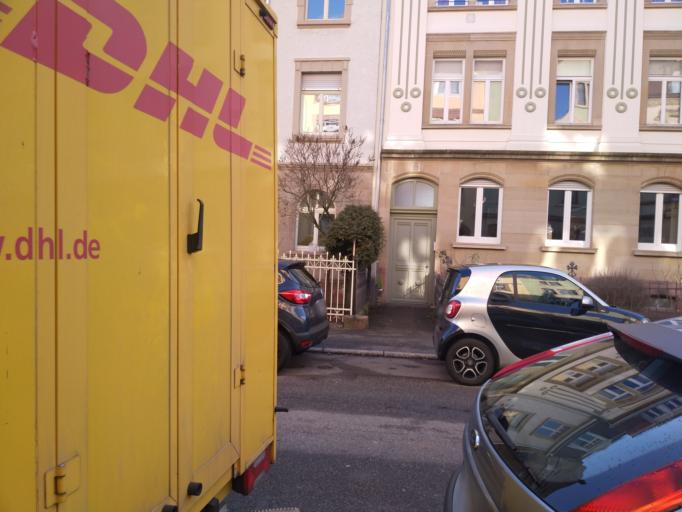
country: DE
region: Baden-Wuerttemberg
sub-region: Karlsruhe Region
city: Pforzheim
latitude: 48.8855
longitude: 8.6915
